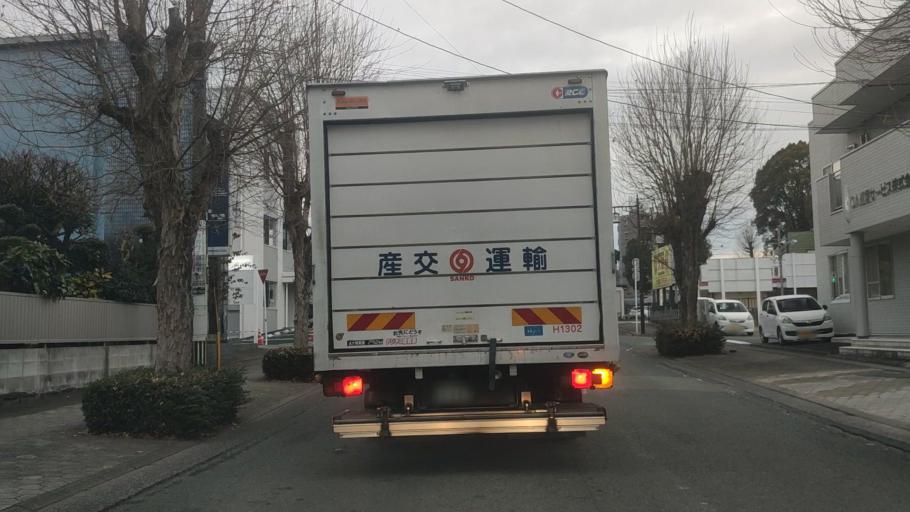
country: JP
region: Kumamoto
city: Kumamoto
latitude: 32.8165
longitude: 130.7526
